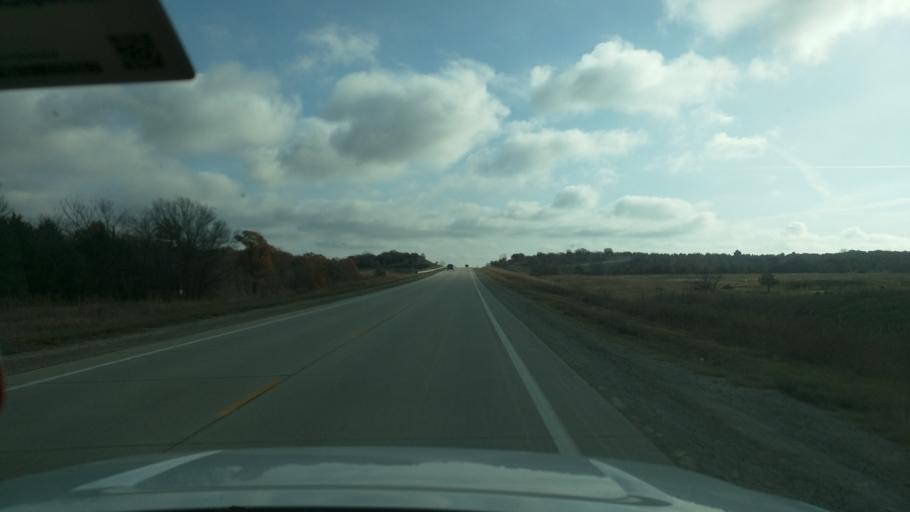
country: US
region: Kansas
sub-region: Chautauqua County
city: Sedan
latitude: 37.0826
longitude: -96.1228
